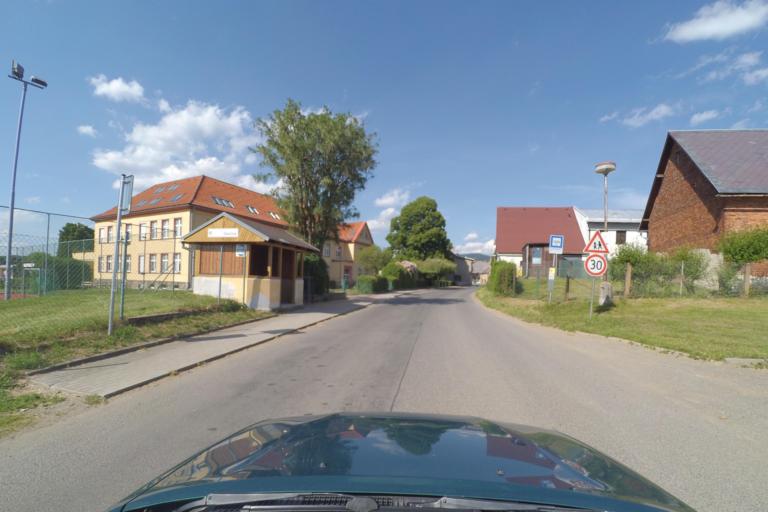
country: CZ
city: Osecna
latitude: 50.6932
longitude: 14.9184
